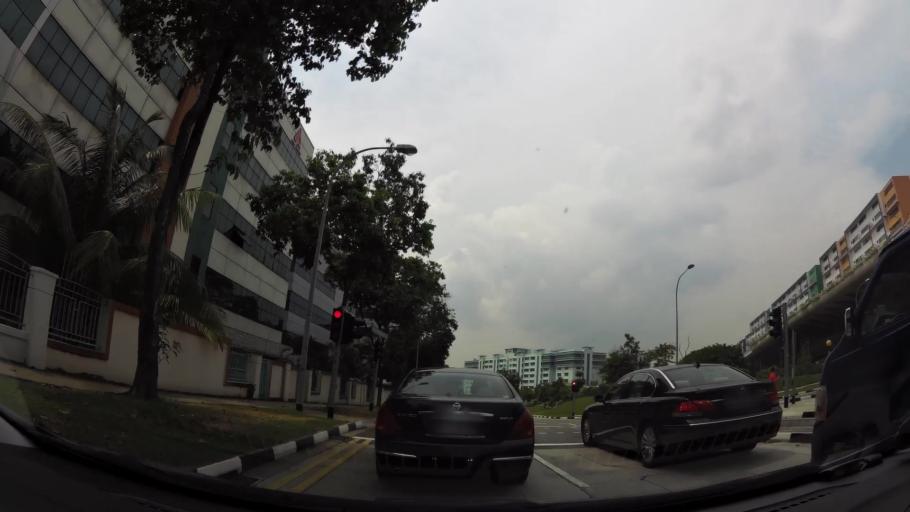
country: SG
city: Singapore
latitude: 1.3371
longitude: 103.9079
